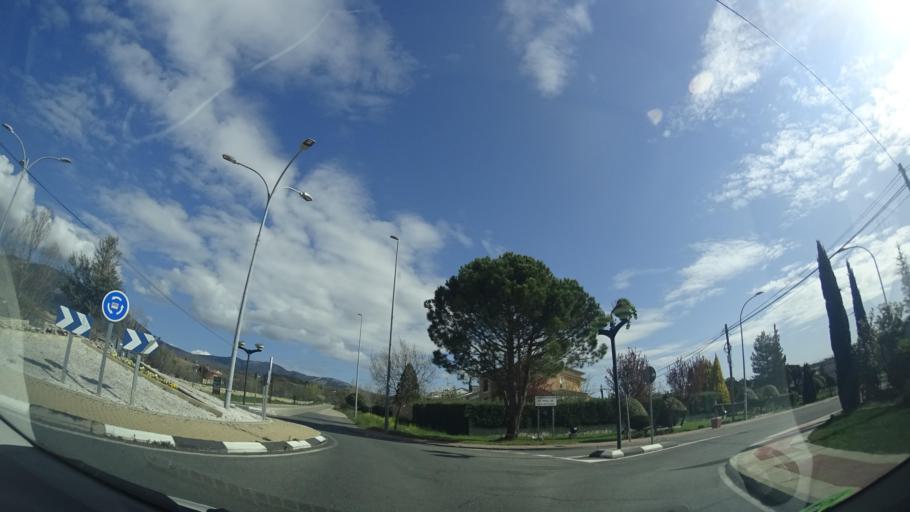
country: ES
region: Madrid
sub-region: Provincia de Madrid
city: Miraflores de la Sierra
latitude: 40.7648
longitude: -3.7816
